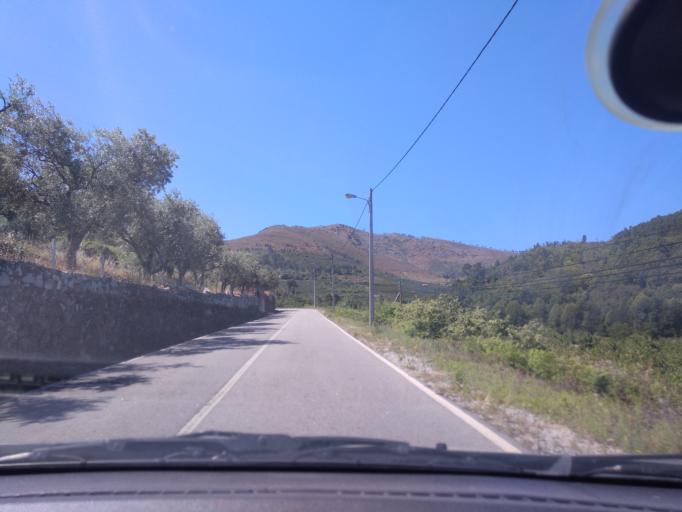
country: PT
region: Castelo Branco
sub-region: Concelho do Fundao
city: Fundao
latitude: 40.1266
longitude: -7.4872
